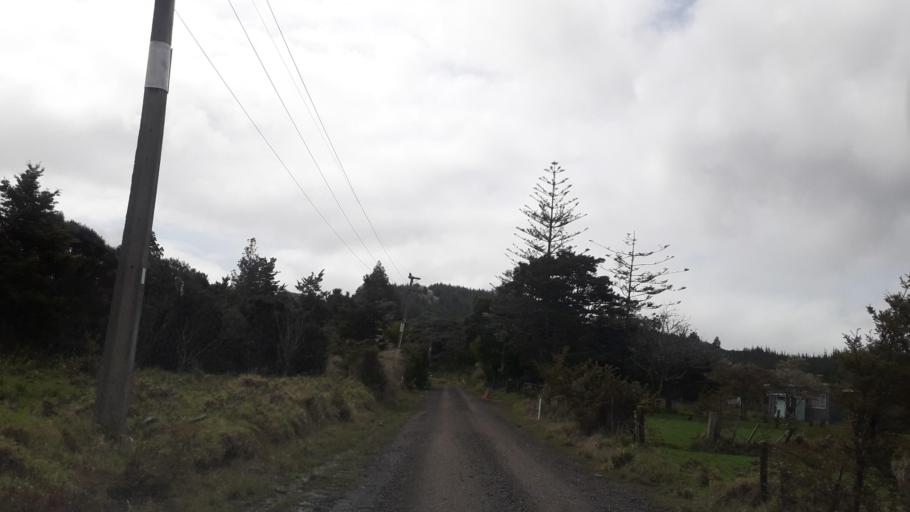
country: NZ
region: Northland
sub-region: Far North District
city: Kaitaia
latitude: -35.3778
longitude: 173.4110
